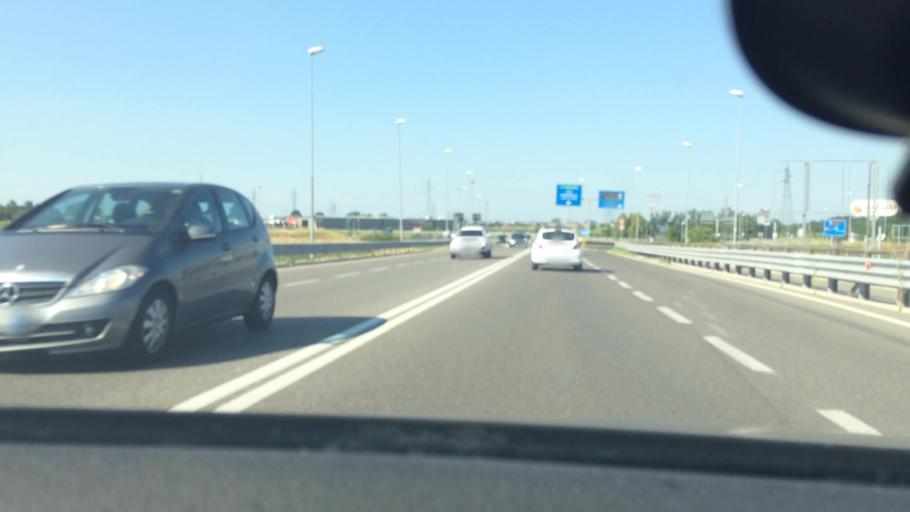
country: IT
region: Lombardy
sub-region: Provincia di Lodi
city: San Rocco al Porto
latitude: 45.0677
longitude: 9.7084
